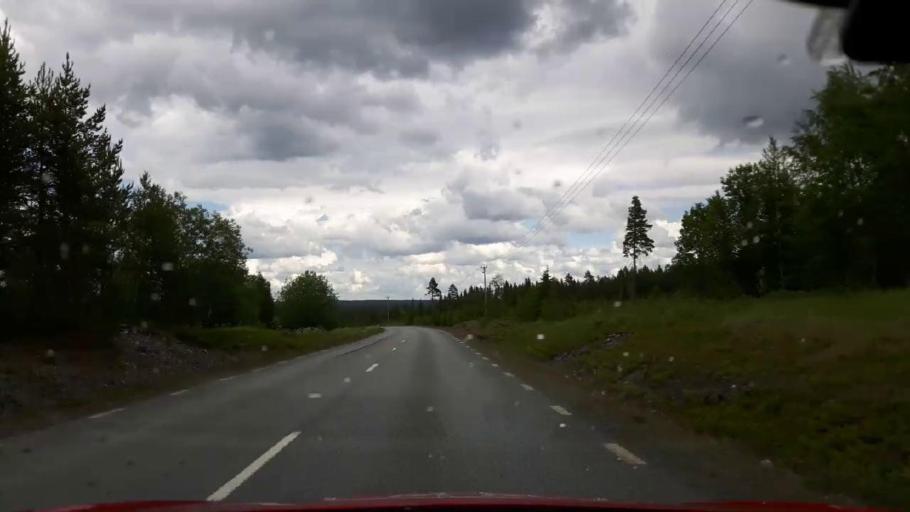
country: SE
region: Jaemtland
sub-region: Krokoms Kommun
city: Krokom
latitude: 63.5427
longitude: 14.2704
